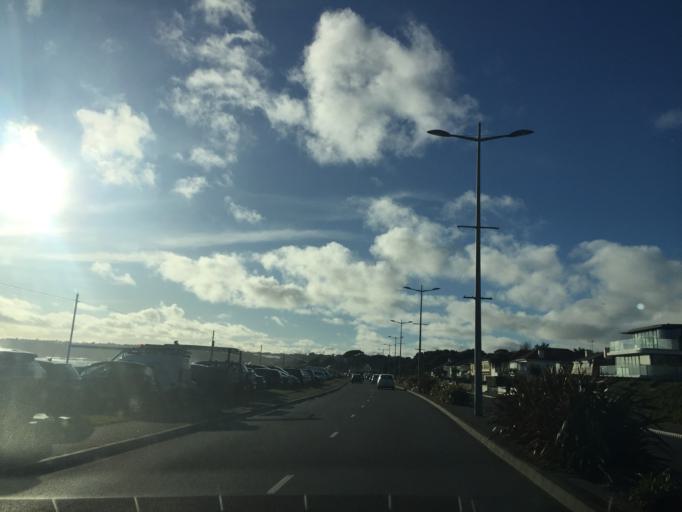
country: JE
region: St Helier
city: Saint Helier
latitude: 49.1956
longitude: -2.1334
